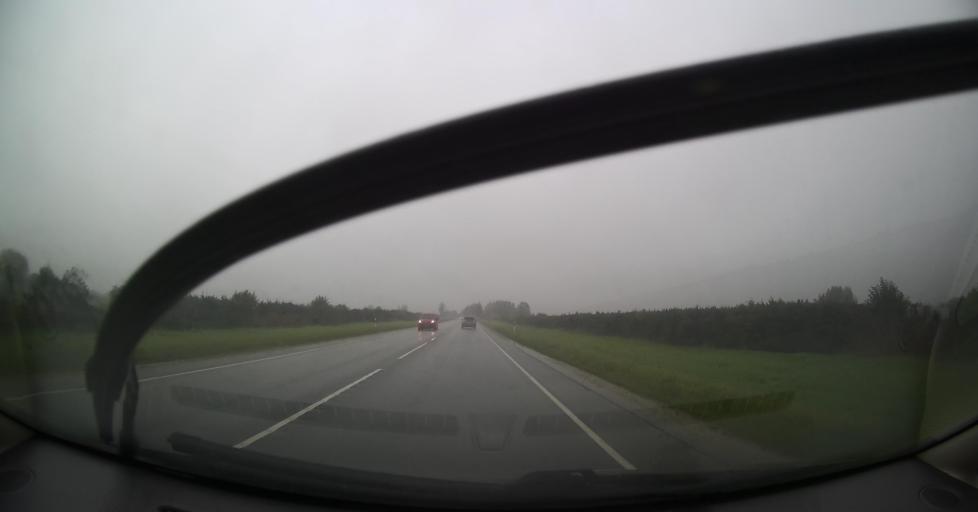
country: EE
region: Jaervamaa
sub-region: Paide linn
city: Paide
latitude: 58.8420
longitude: 25.7410
